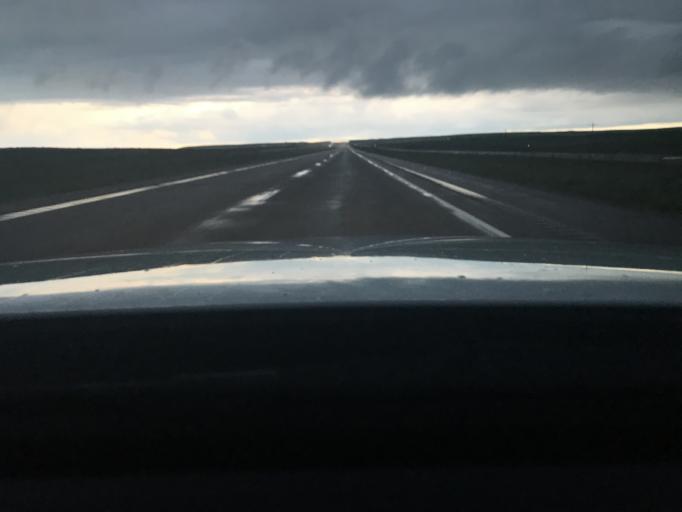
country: US
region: Wyoming
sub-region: Platte County
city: Wheatland
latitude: 41.6789
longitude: -104.8342
